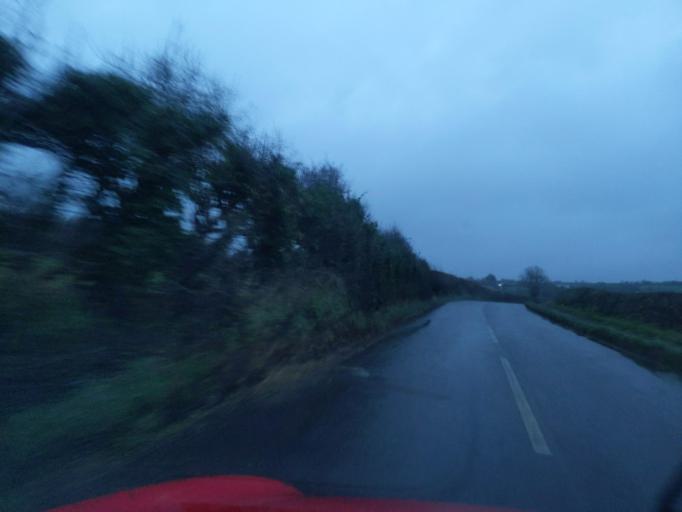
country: GB
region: England
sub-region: Cornwall
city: Saltash
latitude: 50.3632
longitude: -4.2643
